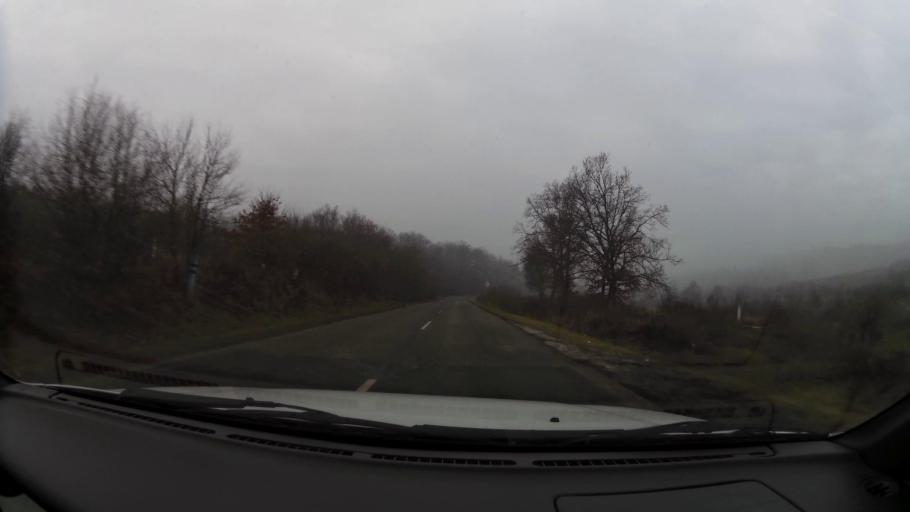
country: HU
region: Borsod-Abauj-Zemplen
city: Rudabanya
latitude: 48.3541
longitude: 20.6361
